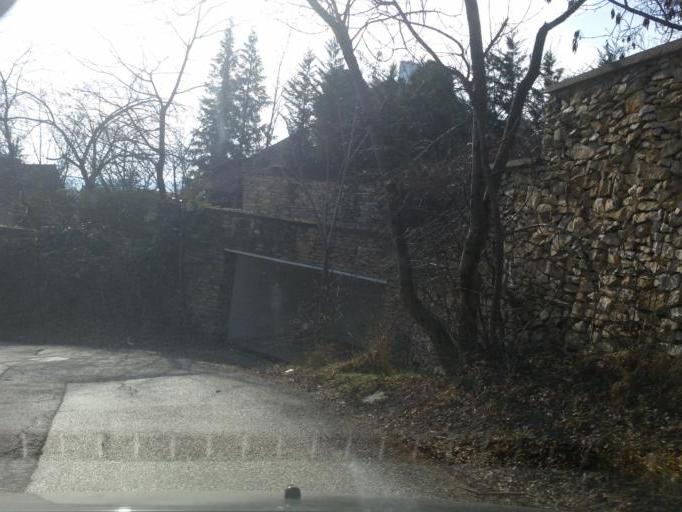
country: HU
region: Budapest
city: Budapest II. keruelet
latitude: 47.5336
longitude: 19.0008
